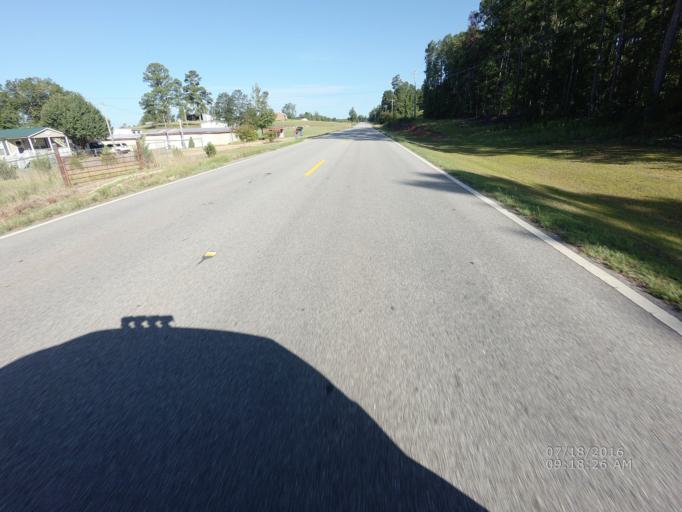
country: US
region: Alabama
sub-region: Chambers County
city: Huguley
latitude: 32.8595
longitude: -85.2844
